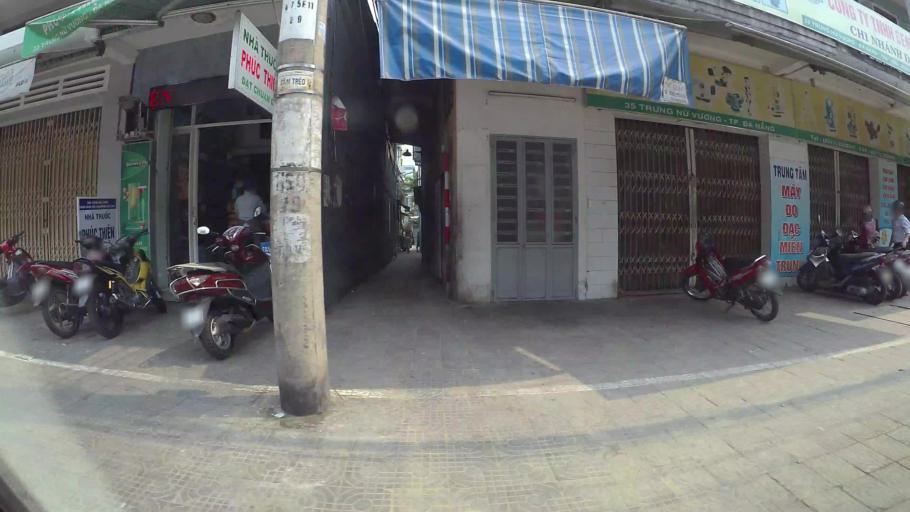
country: VN
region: Da Nang
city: Da Nang
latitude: 16.0592
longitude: 108.2218
